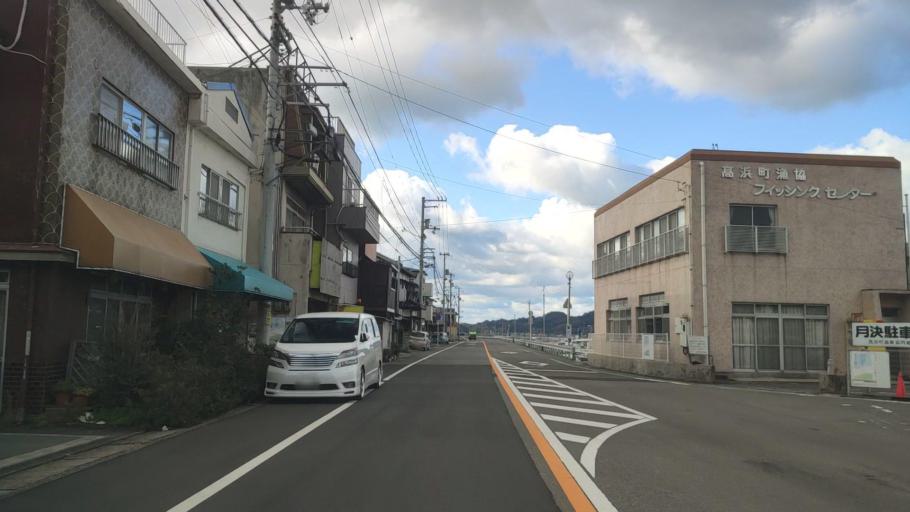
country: JP
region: Ehime
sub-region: Shikoku-chuo Shi
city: Matsuyama
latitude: 33.8877
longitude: 132.7030
